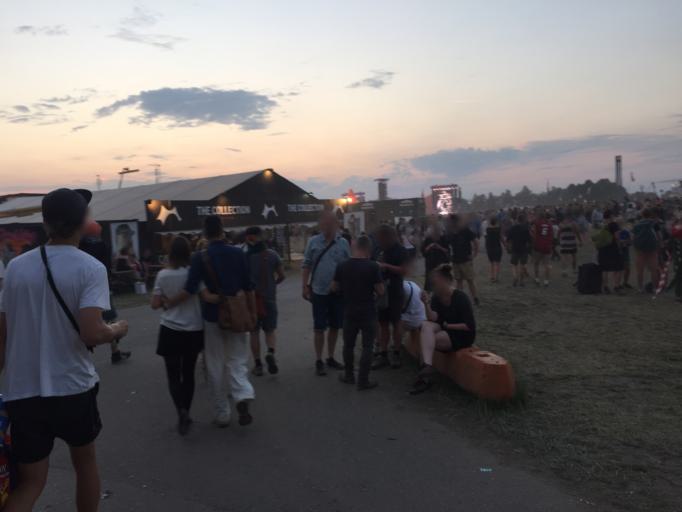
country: DK
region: Zealand
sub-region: Roskilde Kommune
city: Roskilde
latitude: 55.6191
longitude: 12.0790
